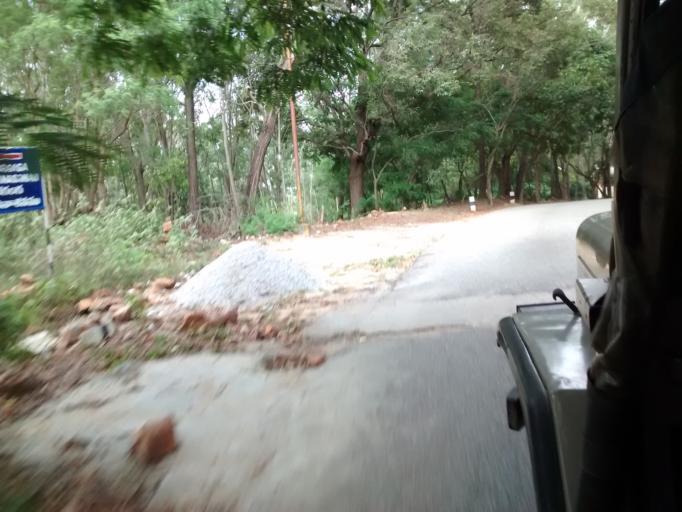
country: IN
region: Andhra Pradesh
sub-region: Chittoor
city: Tirumala
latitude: 13.7049
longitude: 79.3437
